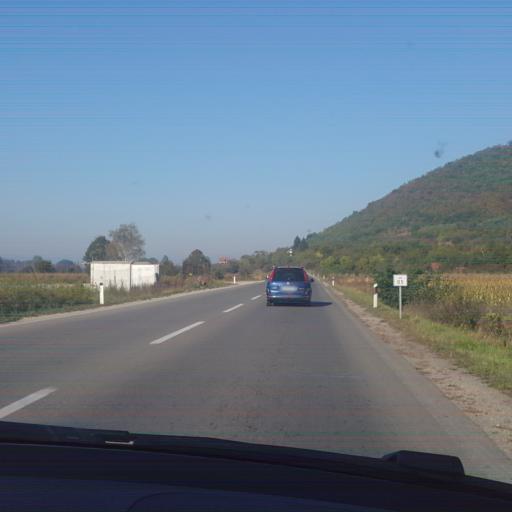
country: RS
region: Central Serbia
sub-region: Toplicki Okrug
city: Prokuplje
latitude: 43.2342
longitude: 21.5236
